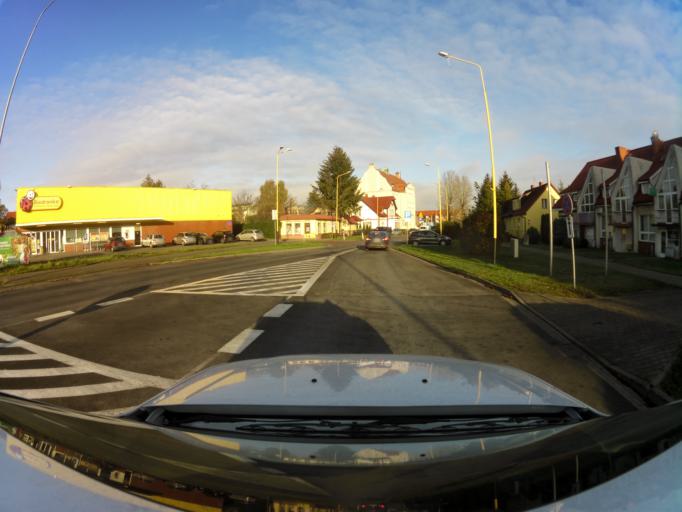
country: PL
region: West Pomeranian Voivodeship
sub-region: Powiat gryficki
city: Gryfice
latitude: 53.9117
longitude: 15.1959
